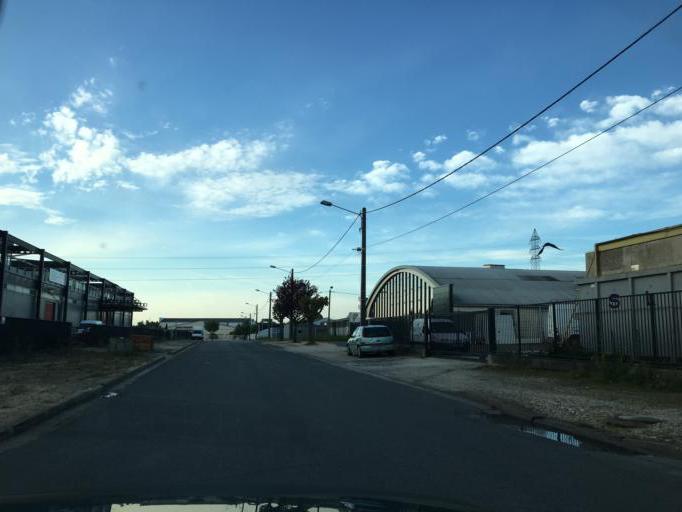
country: FR
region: Centre
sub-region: Departement du Loiret
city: Saint-Jean-de-la-Ruelle
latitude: 47.9089
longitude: 1.8517
